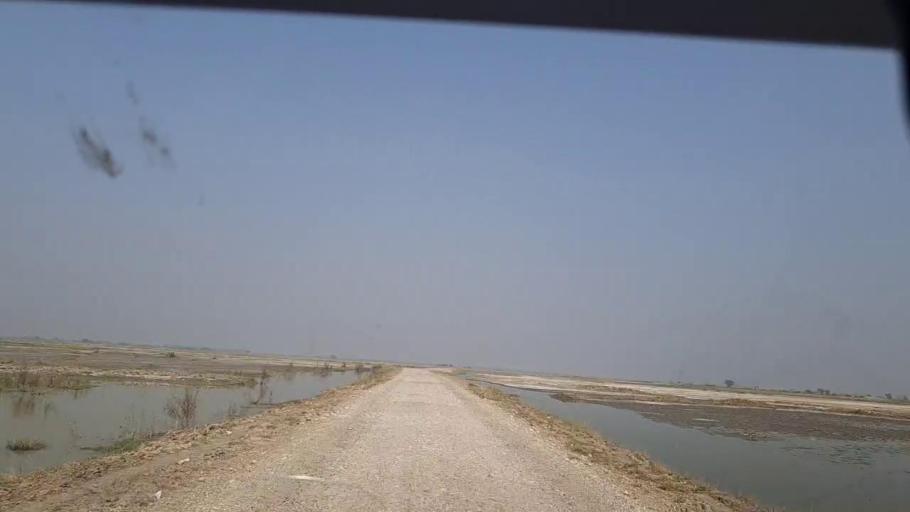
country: PK
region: Sindh
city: Shikarpur
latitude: 28.0439
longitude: 68.6518
